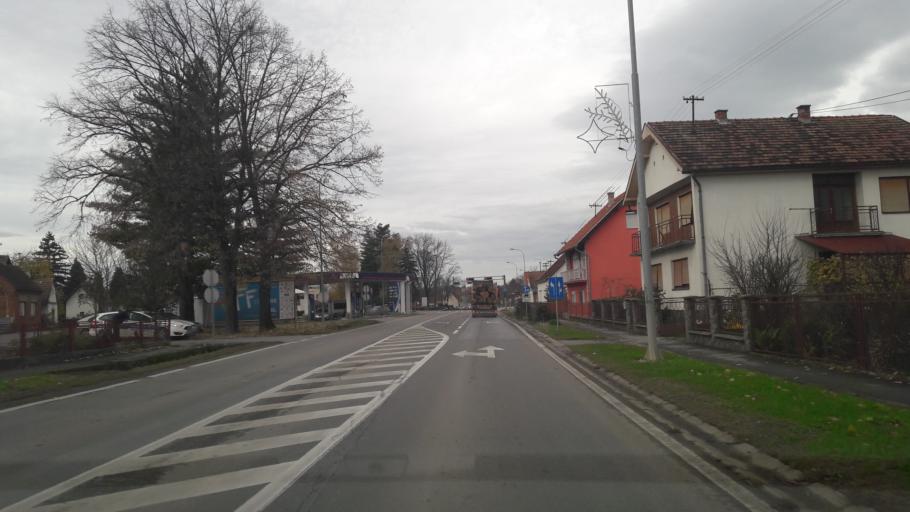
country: HR
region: Virovitick-Podravska
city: Orahovica
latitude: 45.5479
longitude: 17.9038
